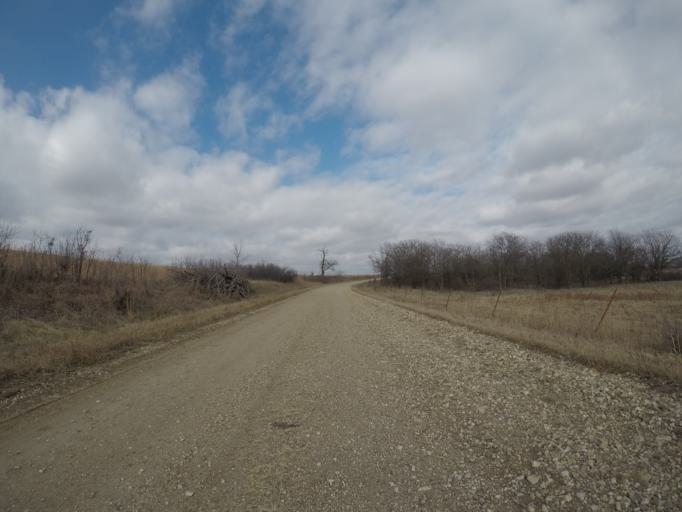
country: US
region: Kansas
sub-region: Morris County
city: Council Grove
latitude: 38.7750
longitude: -96.3527
